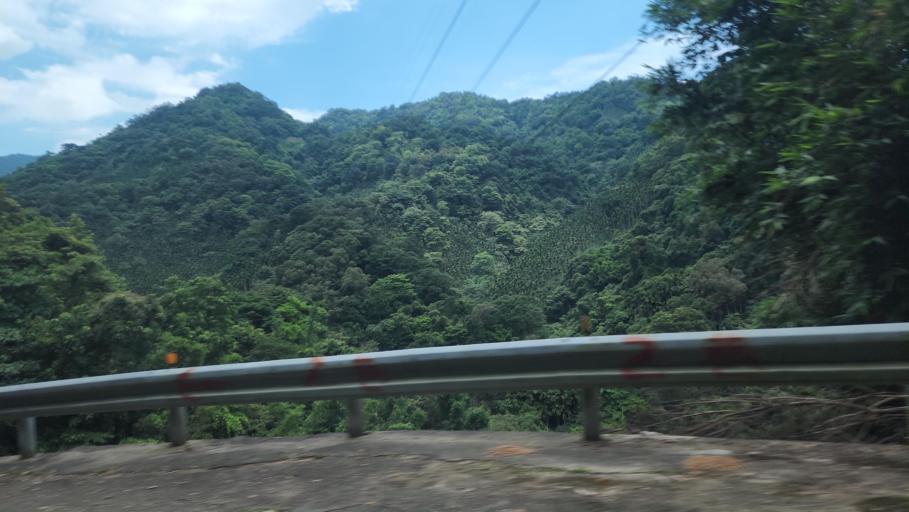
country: TW
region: Taipei
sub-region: Taipei
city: Banqiao
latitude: 24.9050
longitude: 121.4338
